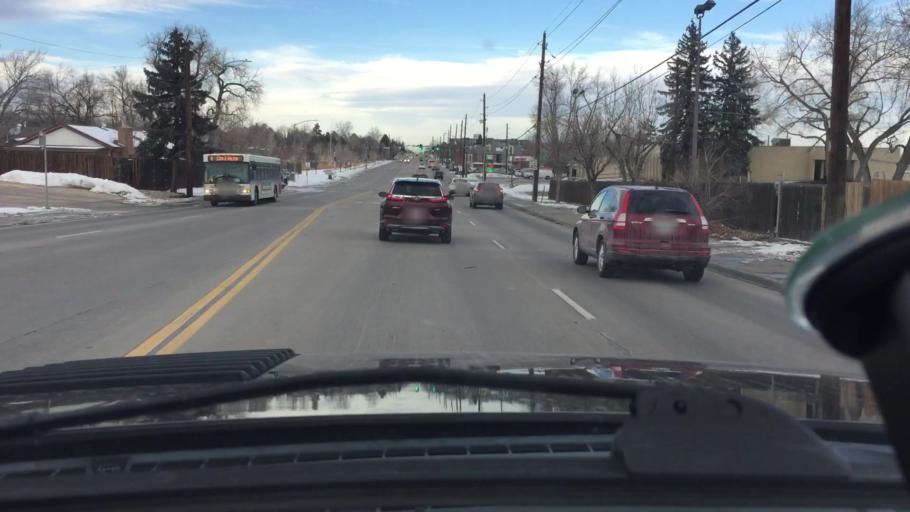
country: US
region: Colorado
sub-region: Adams County
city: Northglenn
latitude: 39.8863
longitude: -104.9966
